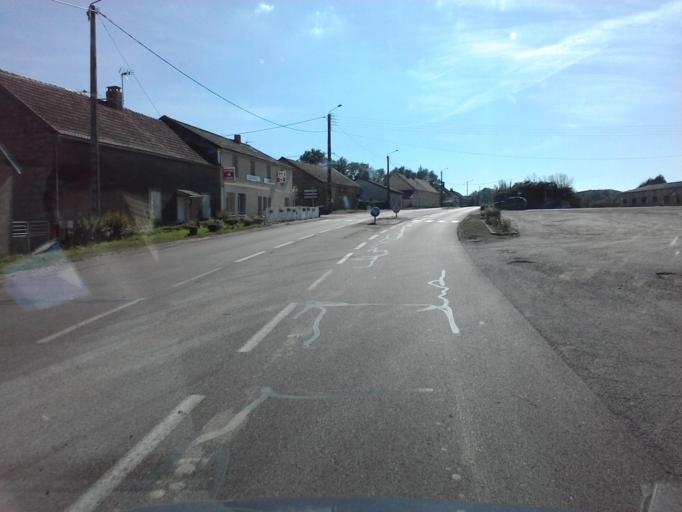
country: FR
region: Bourgogne
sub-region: Departement de la Cote-d'Or
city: Saulieu
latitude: 47.3423
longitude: 4.1974
